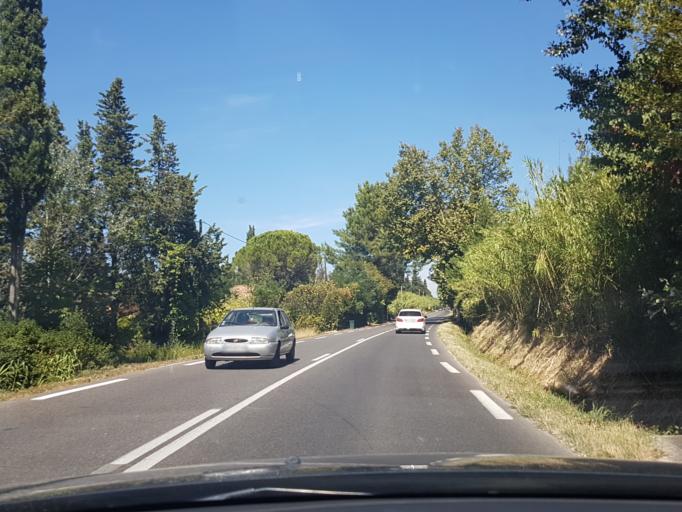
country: FR
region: Provence-Alpes-Cote d'Azur
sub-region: Departement des Bouches-du-Rhone
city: Eyragues
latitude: 43.8249
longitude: 4.8358
